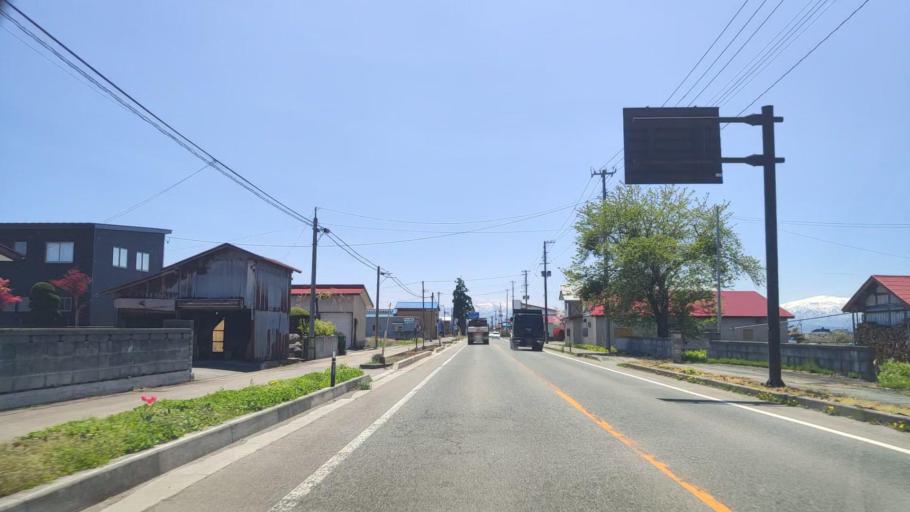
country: JP
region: Yamagata
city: Shinjo
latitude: 38.8161
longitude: 140.3250
